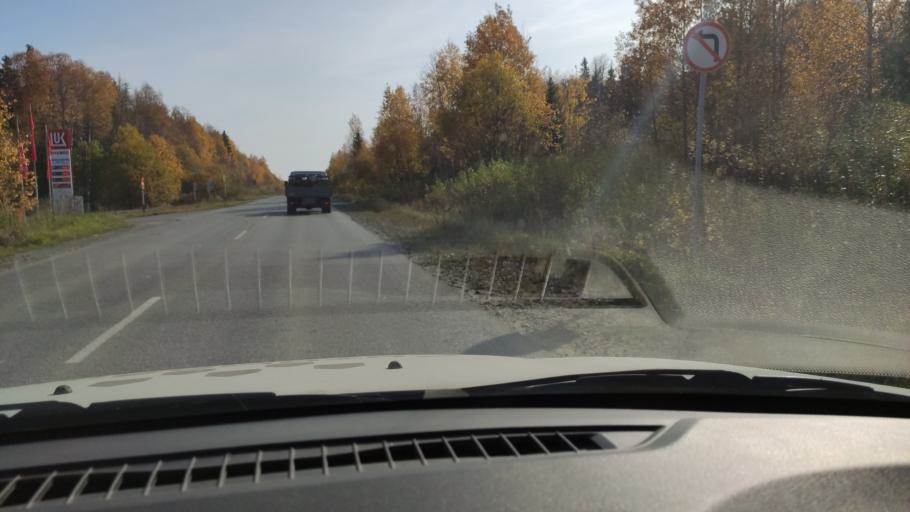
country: RU
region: Perm
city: Novyye Lyady
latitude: 58.0311
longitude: 56.6170
